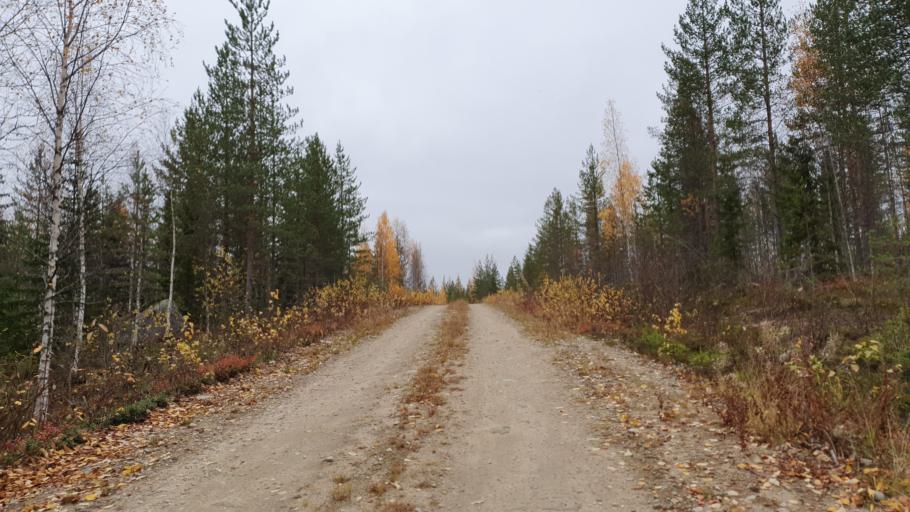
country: FI
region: Kainuu
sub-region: Kehys-Kainuu
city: Kuhmo
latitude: 64.4430
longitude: 29.6153
